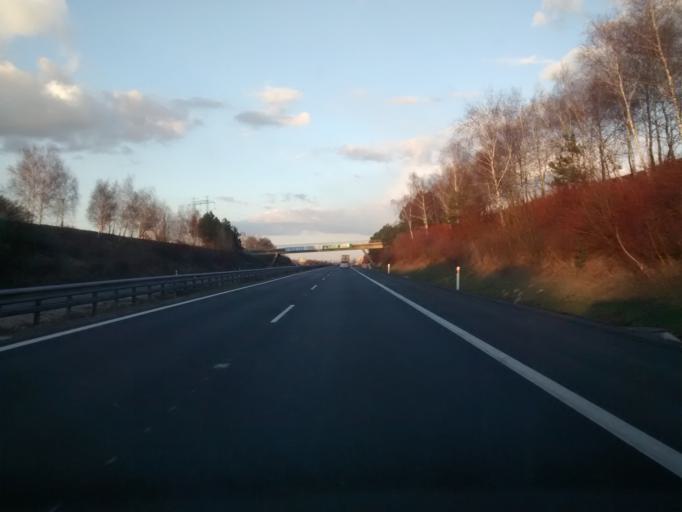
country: CZ
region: Central Bohemia
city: Nehvizdy
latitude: 50.1292
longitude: 14.7472
